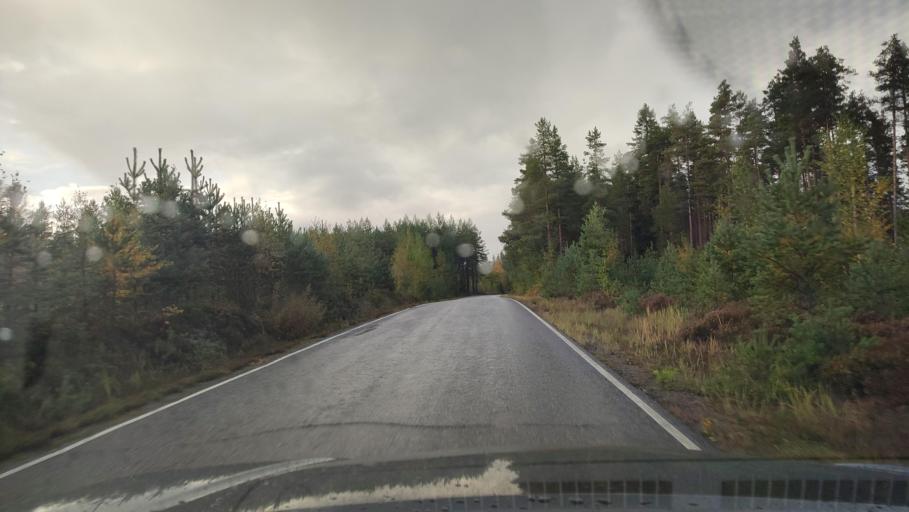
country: FI
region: Southern Ostrobothnia
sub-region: Suupohja
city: Karijoki
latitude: 62.3182
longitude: 21.6818
